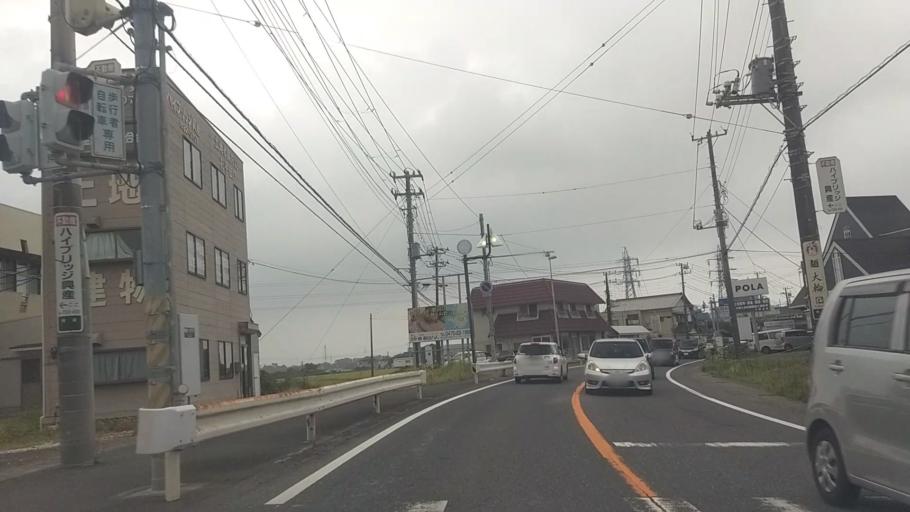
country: JP
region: Chiba
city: Kawaguchi
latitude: 35.1122
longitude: 140.0977
